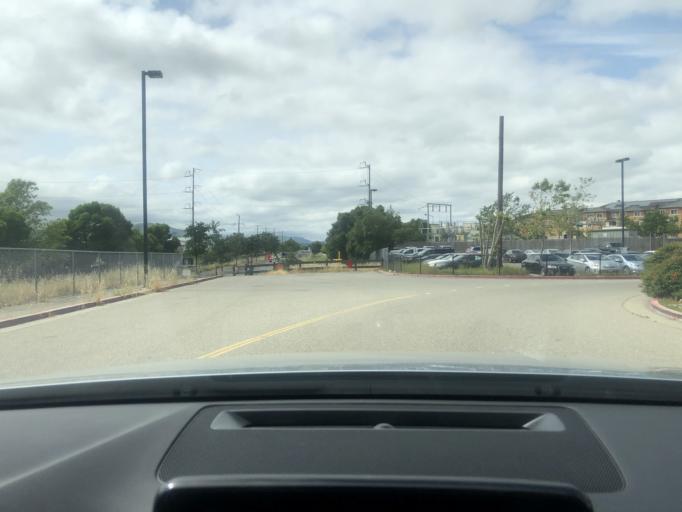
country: US
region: California
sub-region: Alameda County
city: Dublin
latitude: 37.7033
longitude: -121.9003
